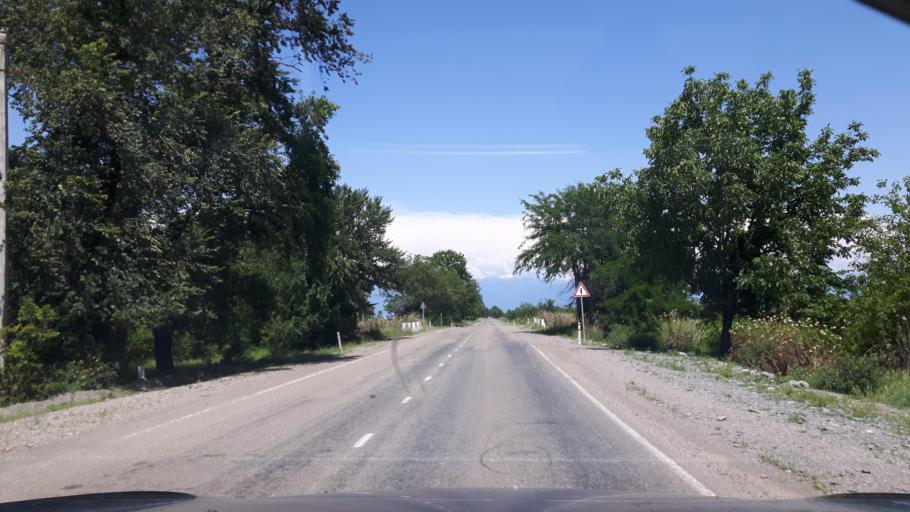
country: GE
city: Tsnori
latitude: 41.6265
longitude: 46.0142
